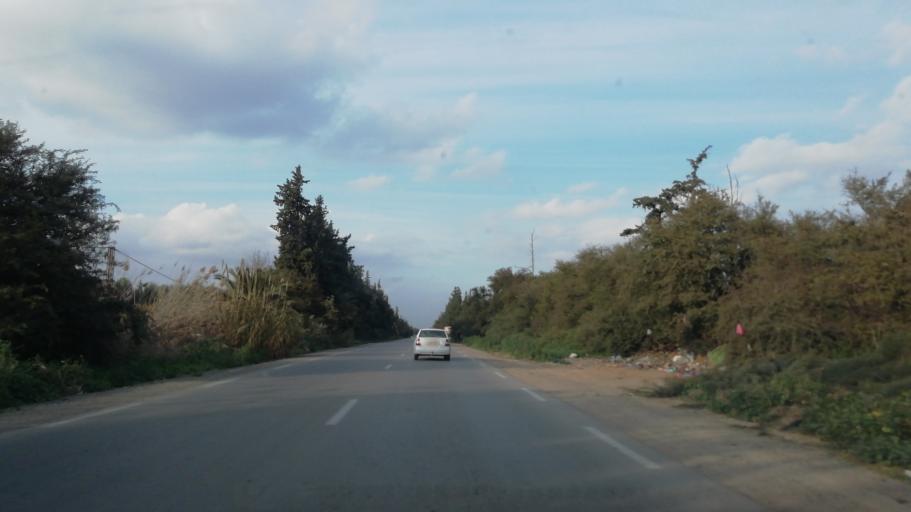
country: DZ
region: Mascara
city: Mascara
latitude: 35.6037
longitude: 0.0526
